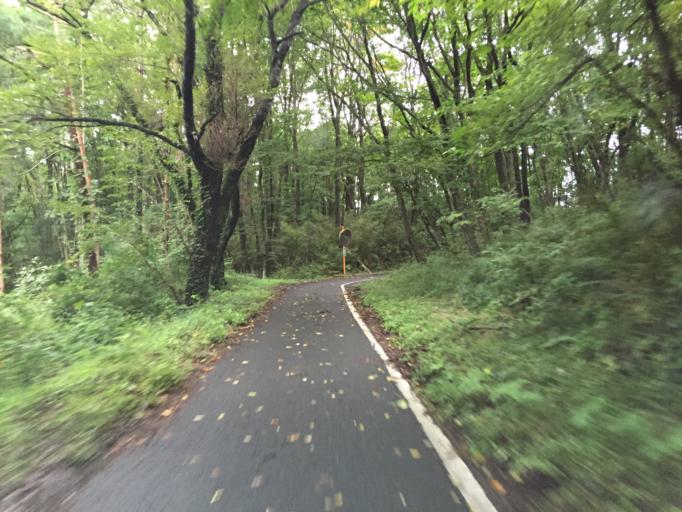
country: JP
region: Fukushima
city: Hobaramachi
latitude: 37.7675
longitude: 140.5236
